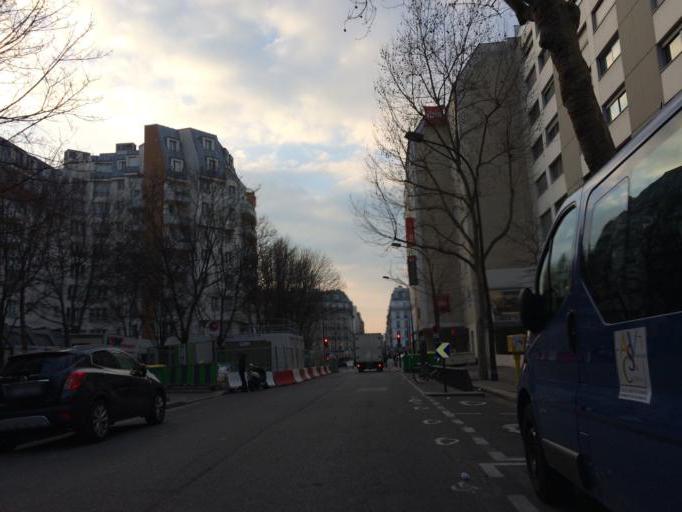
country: FR
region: Ile-de-France
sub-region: Paris
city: Paris
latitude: 48.8790
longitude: 2.3689
